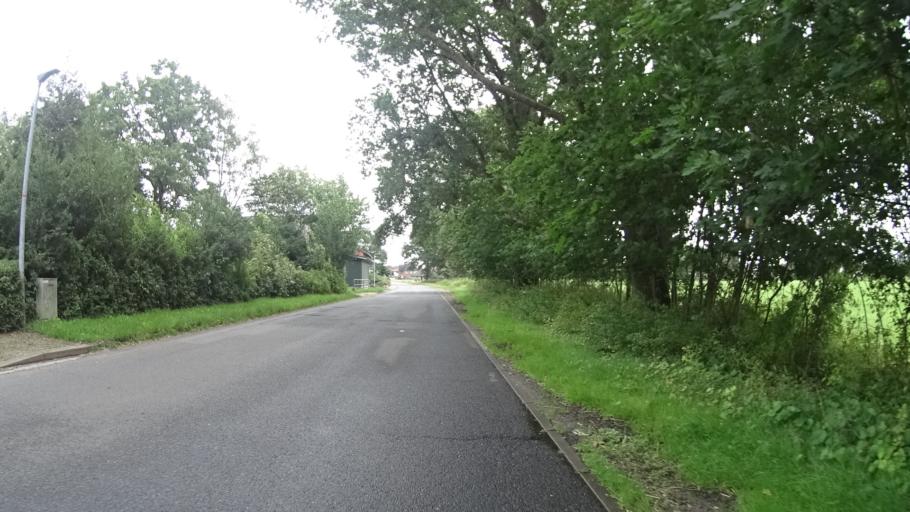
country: DE
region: Schleswig-Holstein
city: Kayhude
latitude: 53.7370
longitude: 10.1478
